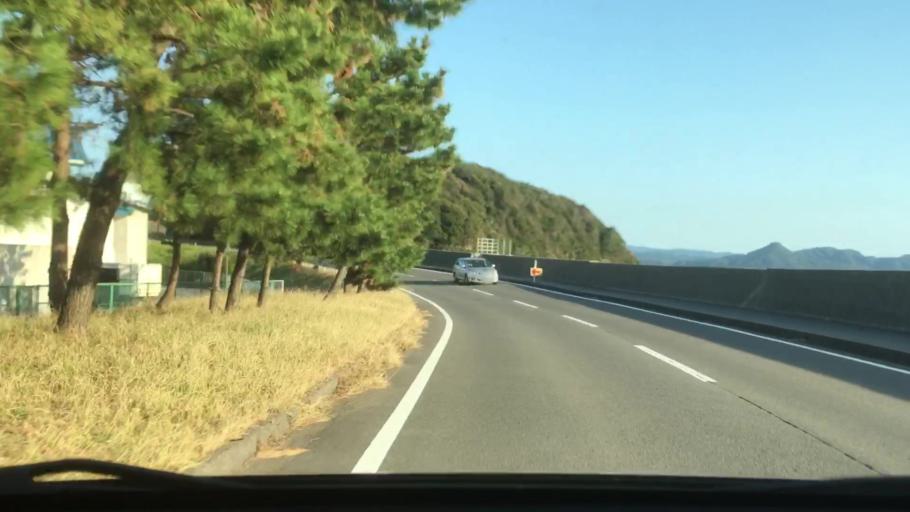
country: JP
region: Nagasaki
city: Sasebo
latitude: 33.0262
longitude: 129.5955
